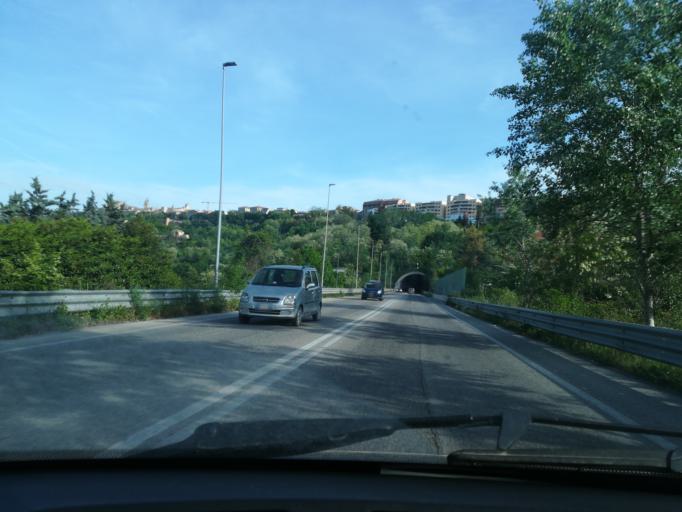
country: IT
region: The Marches
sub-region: Provincia di Macerata
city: Macerata
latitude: 43.3061
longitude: 13.4416
